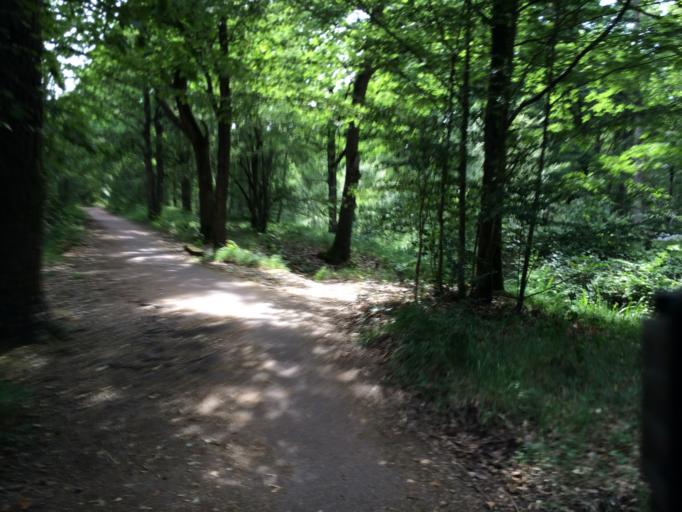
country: FR
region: Ile-de-France
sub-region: Departement de l'Essonne
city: Brunoy
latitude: 48.6734
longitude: 2.4912
